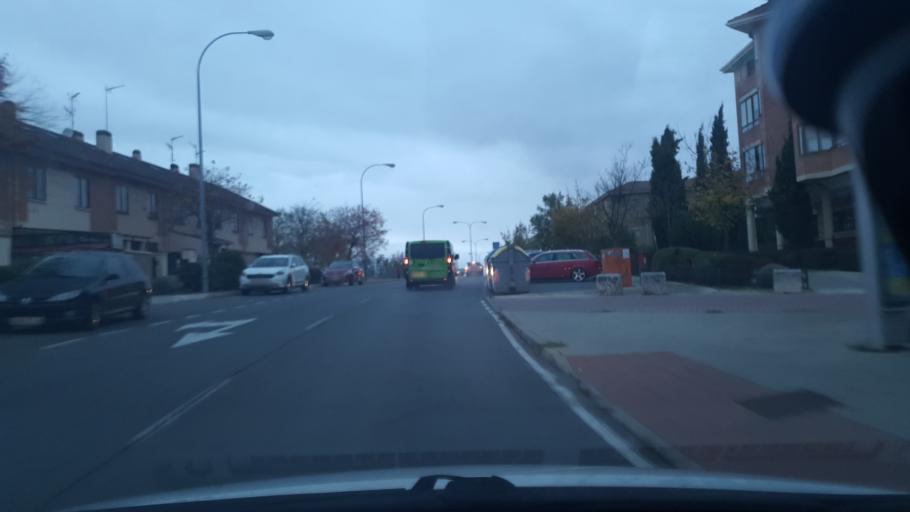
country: ES
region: Castille and Leon
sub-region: Provincia de Segovia
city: Segovia
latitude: 40.9319
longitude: -4.1024
